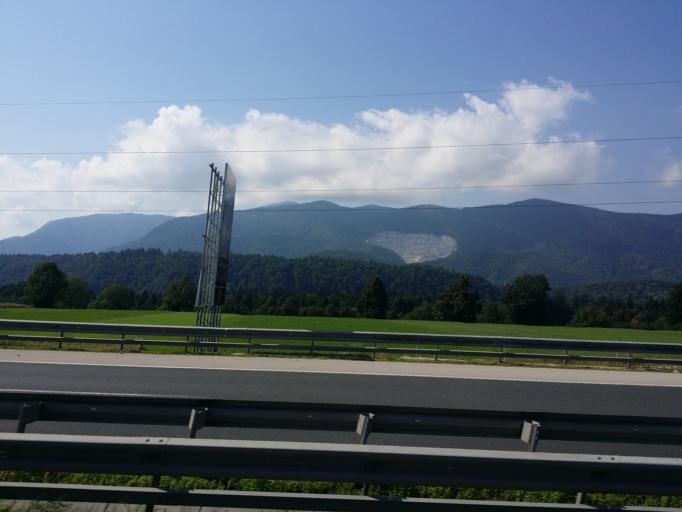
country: SI
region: Radovljica
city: Radovljica
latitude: 46.3299
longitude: 14.2069
